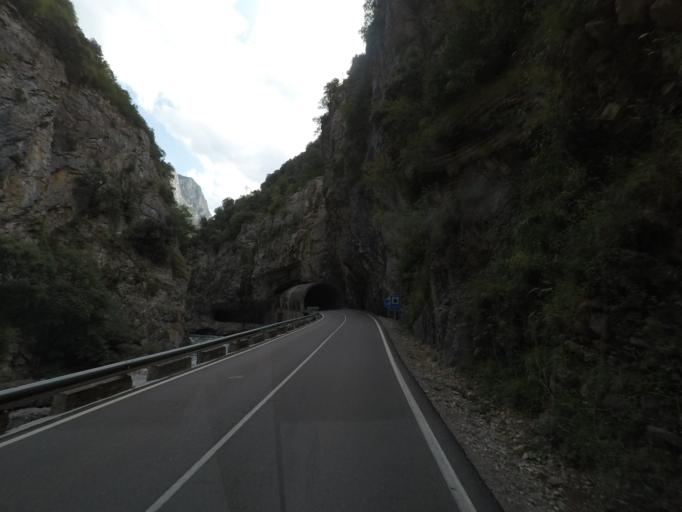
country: ES
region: Aragon
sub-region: Provincia de Huesca
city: Puertolas
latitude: 42.5591
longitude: 0.2044
